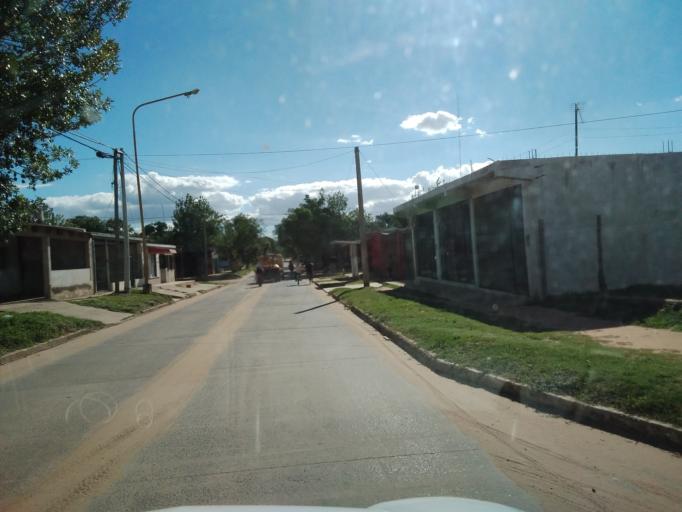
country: AR
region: Corrientes
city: Corrientes
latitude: -27.5044
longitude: -58.8029
